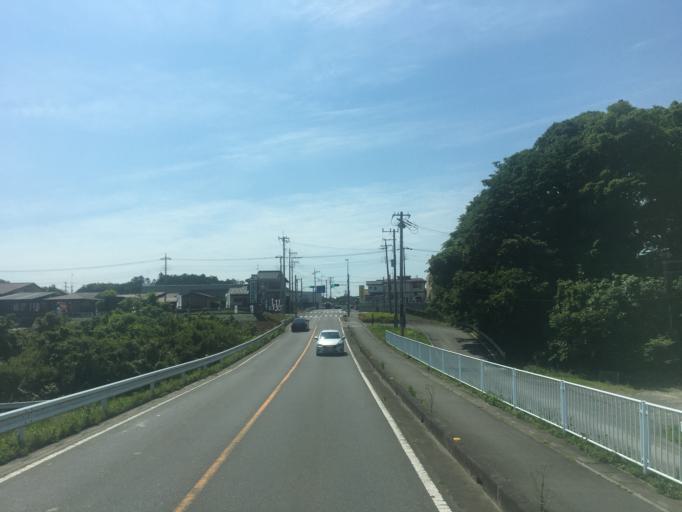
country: JP
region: Saitama
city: Ogawa
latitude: 36.0104
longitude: 139.3012
